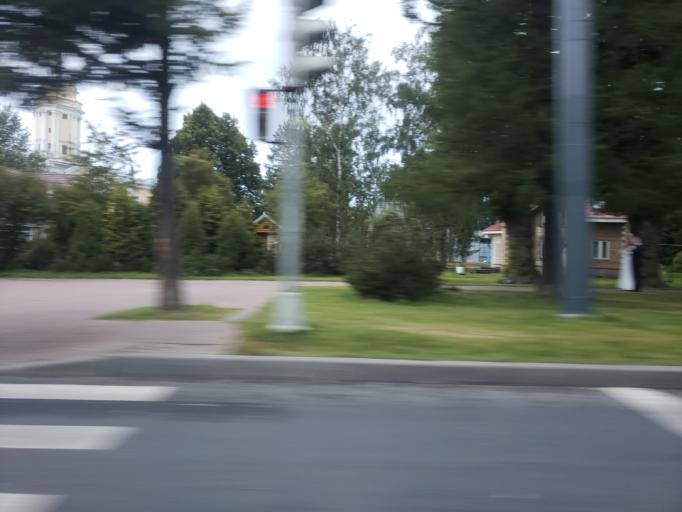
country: RU
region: St.-Petersburg
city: Vasyl'evsky Ostrov
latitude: 59.9314
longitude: 30.2363
